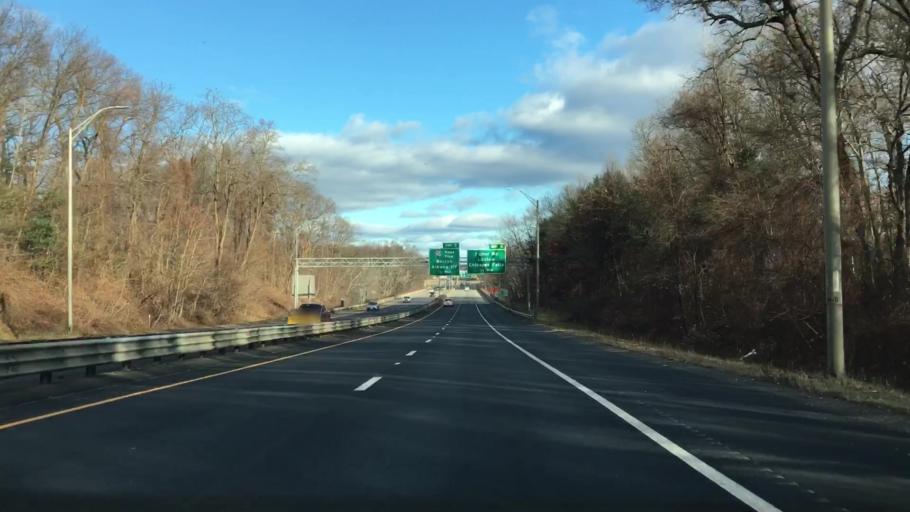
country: US
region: Massachusetts
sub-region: Hampden County
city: North Chicopee
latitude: 42.1548
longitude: -72.5487
